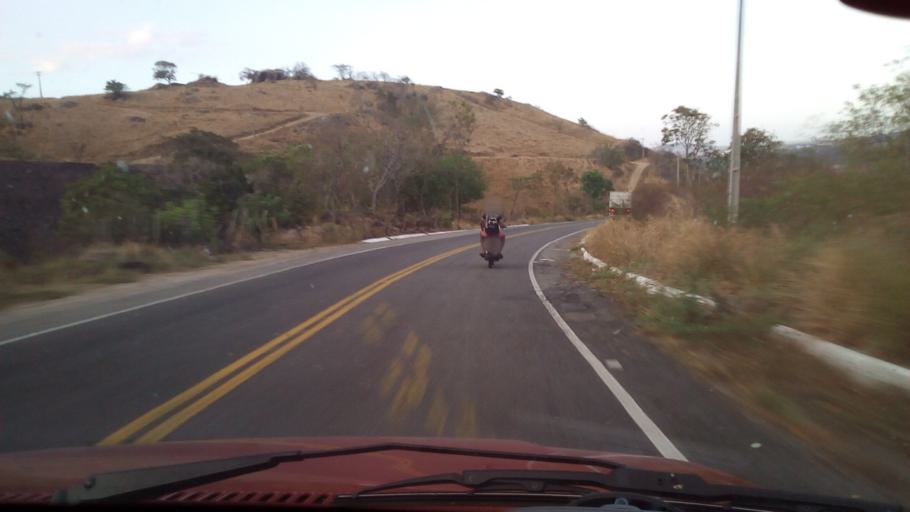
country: BR
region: Paraiba
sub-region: Bananeiras
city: Solanea
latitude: -6.7292
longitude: -35.5544
